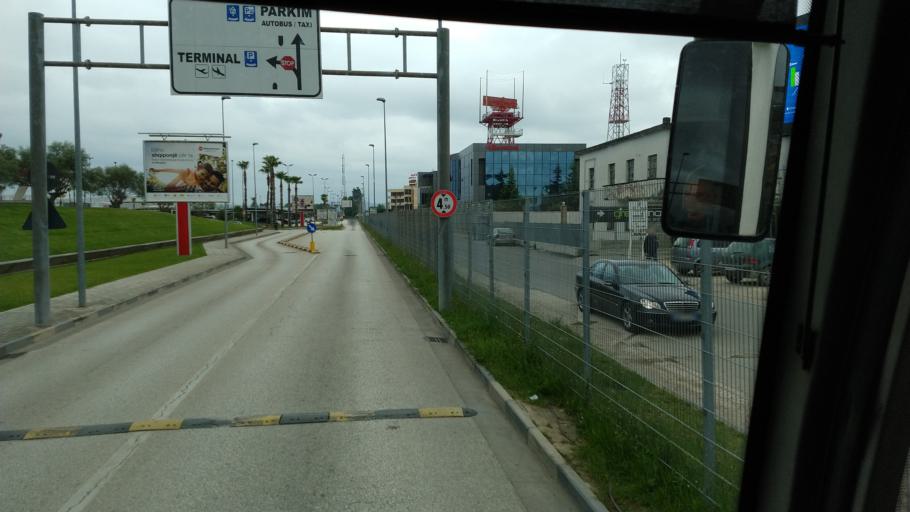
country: AL
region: Tirane
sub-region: Rrethi i Tiranes
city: Preze
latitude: 41.4195
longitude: 19.7126
